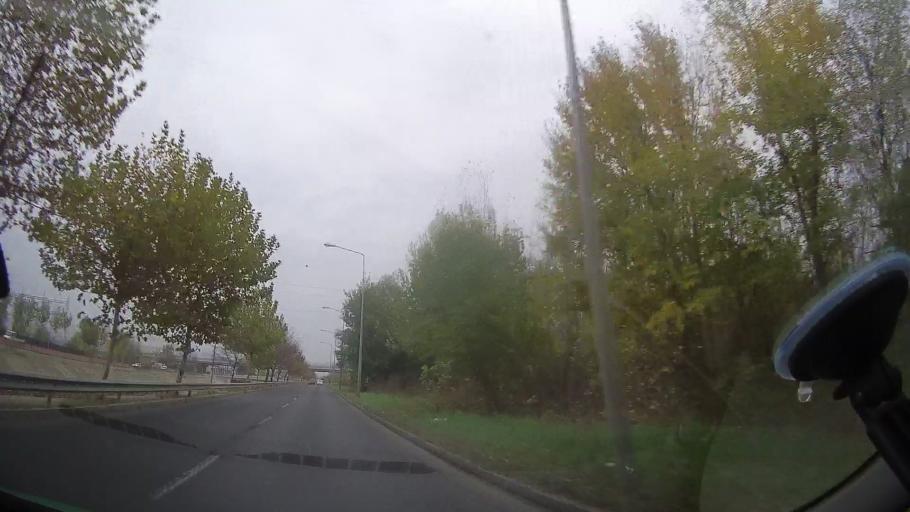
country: RO
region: Ilfov
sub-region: Comuna Popesti-Leordeni
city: Popesti-Leordeni
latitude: 44.3997
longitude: 26.1567
